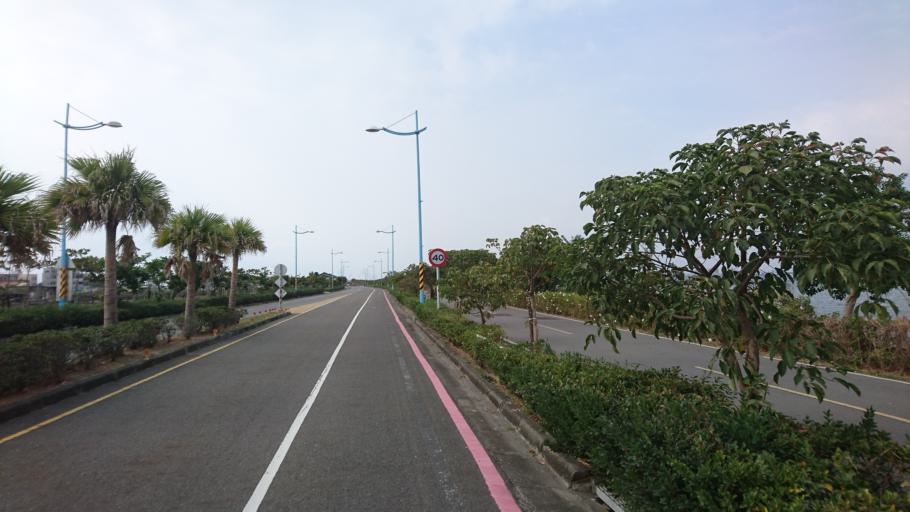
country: TW
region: Taiwan
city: Fengshan
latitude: 22.4334
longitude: 120.4831
